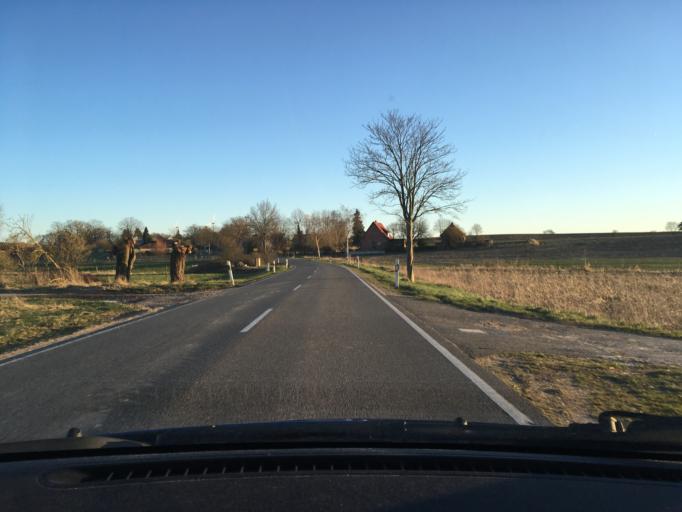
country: DE
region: Lower Saxony
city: Dahlem
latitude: 53.2186
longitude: 10.7545
